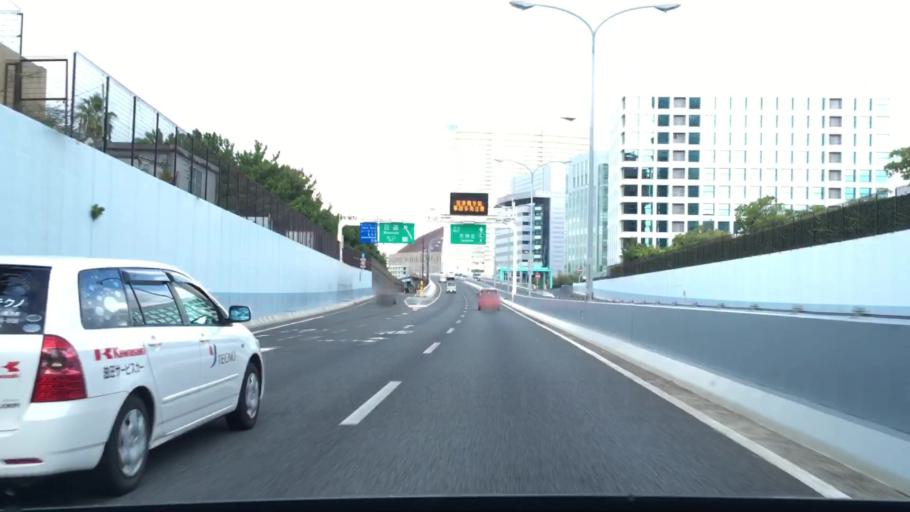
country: JP
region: Fukuoka
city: Fukuoka-shi
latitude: 33.5941
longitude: 130.3519
